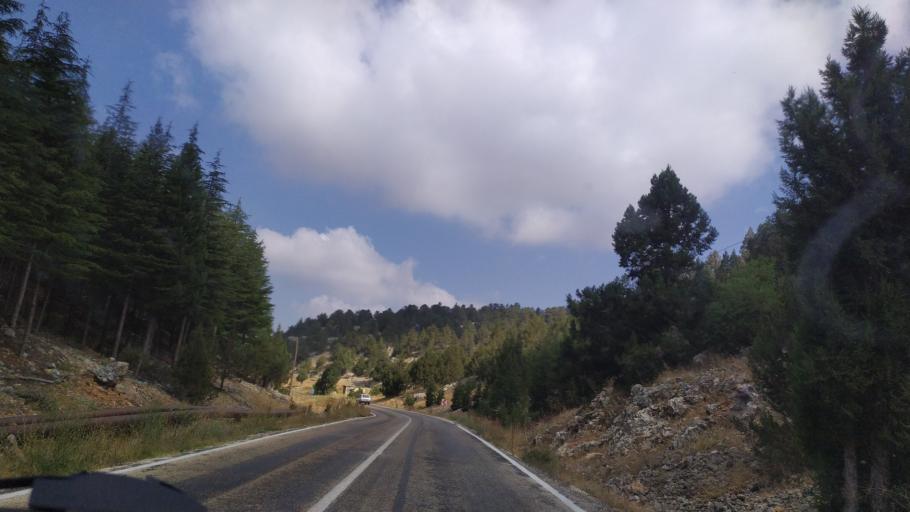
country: TR
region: Mersin
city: Kirobasi
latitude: 36.6134
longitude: 33.8791
